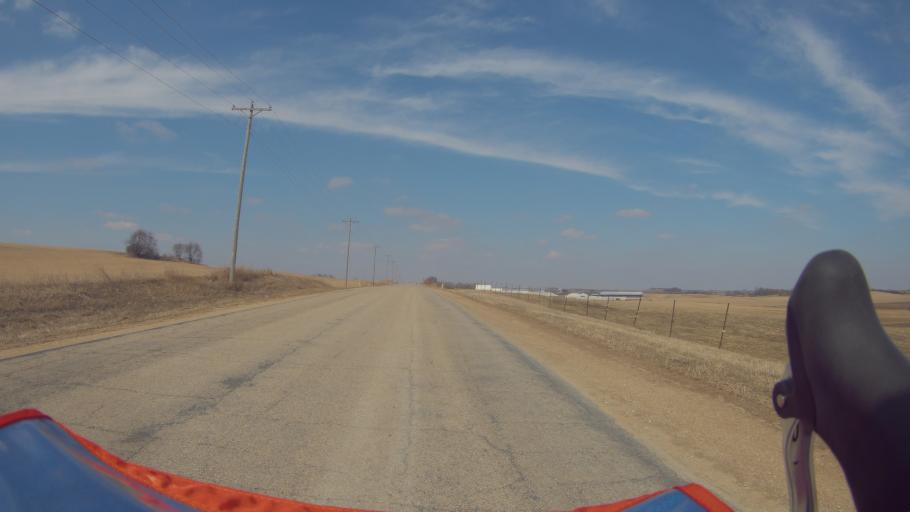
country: US
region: Wisconsin
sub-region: Dane County
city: Middleton
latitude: 43.1301
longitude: -89.4917
